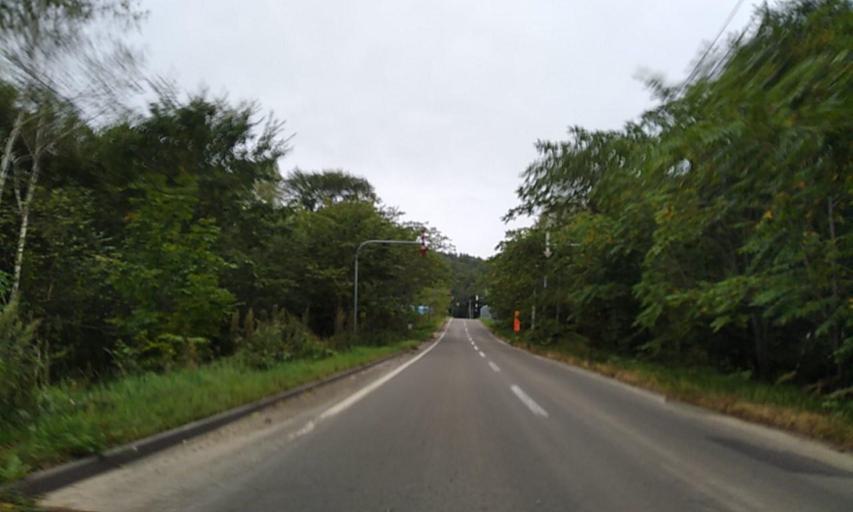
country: JP
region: Hokkaido
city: Bihoro
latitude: 43.6259
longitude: 144.1072
